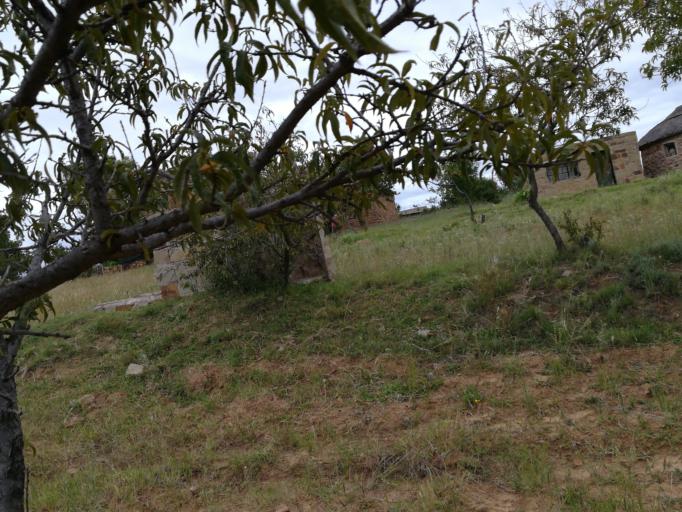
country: LS
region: Quthing
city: Quthing
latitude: -30.3361
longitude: 27.5302
